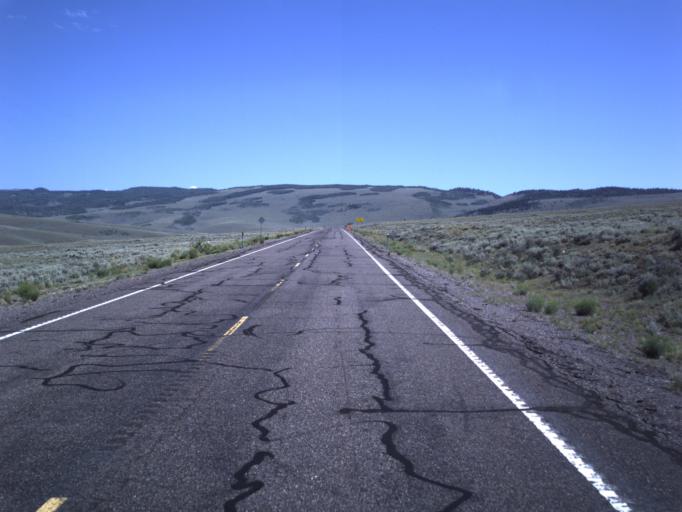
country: US
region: Utah
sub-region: Wayne County
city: Loa
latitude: 38.5624
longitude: -111.5015
